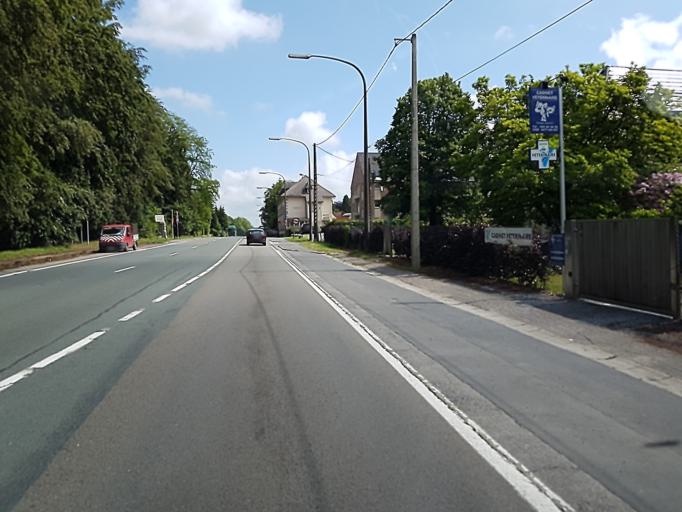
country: BE
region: Wallonia
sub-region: Province du Hainaut
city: Mons
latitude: 50.5044
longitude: 3.9969
